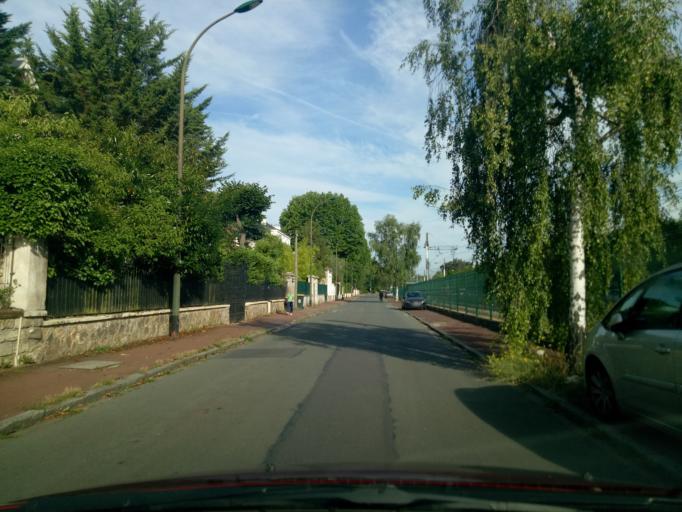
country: FR
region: Ile-de-France
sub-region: Departement des Yvelines
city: Le Vesinet
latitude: 48.8907
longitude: 2.1321
